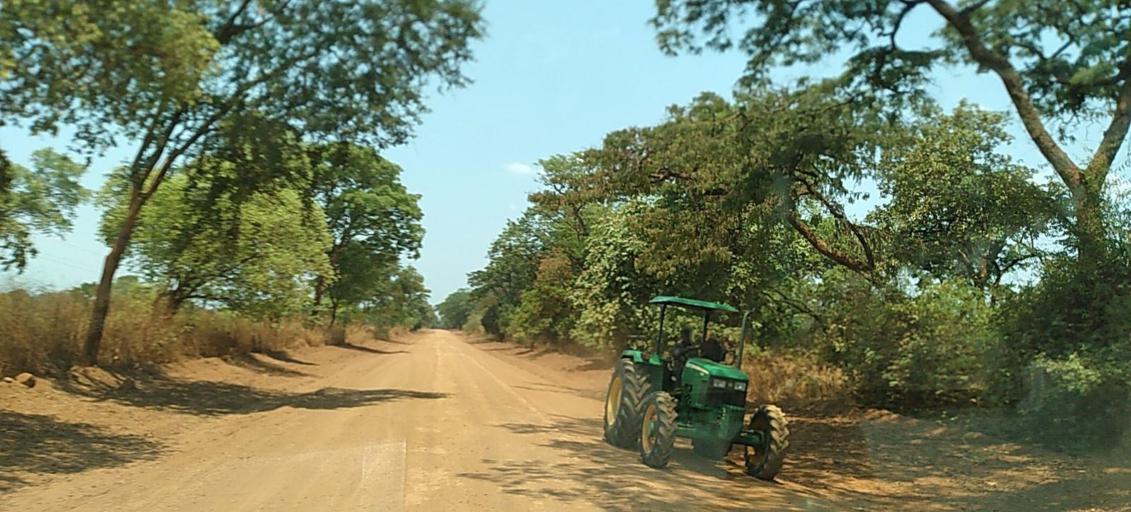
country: ZM
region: Copperbelt
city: Mpongwe
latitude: -13.5163
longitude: 27.9981
